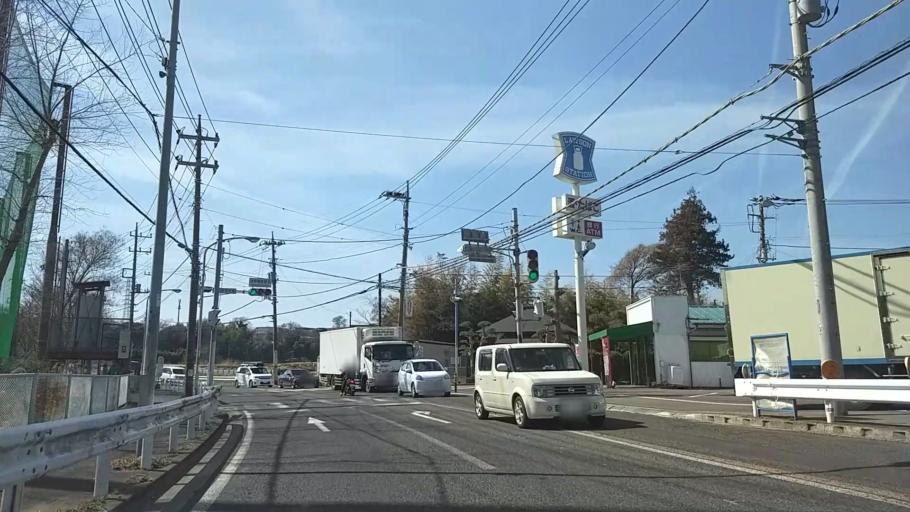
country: JP
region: Kanagawa
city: Fujisawa
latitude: 35.3816
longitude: 139.4917
